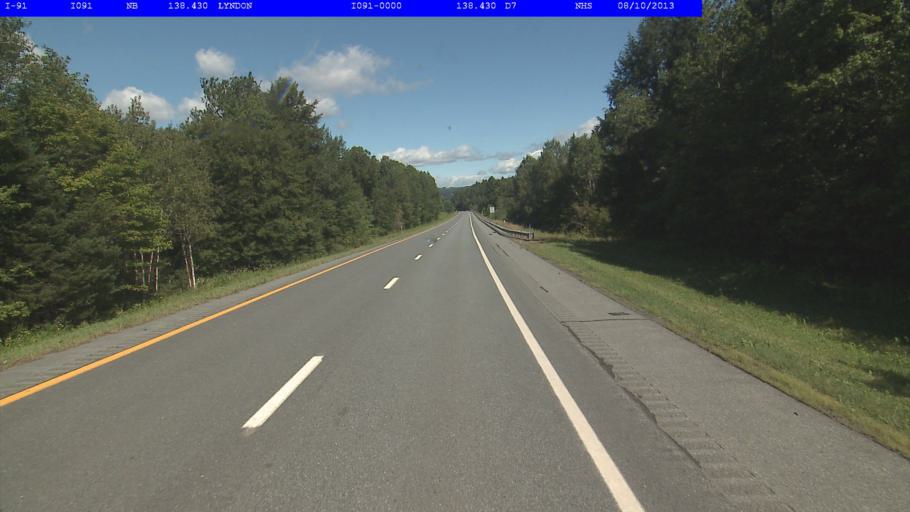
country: US
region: Vermont
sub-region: Caledonia County
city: Lyndonville
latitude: 44.5340
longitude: -72.0173
